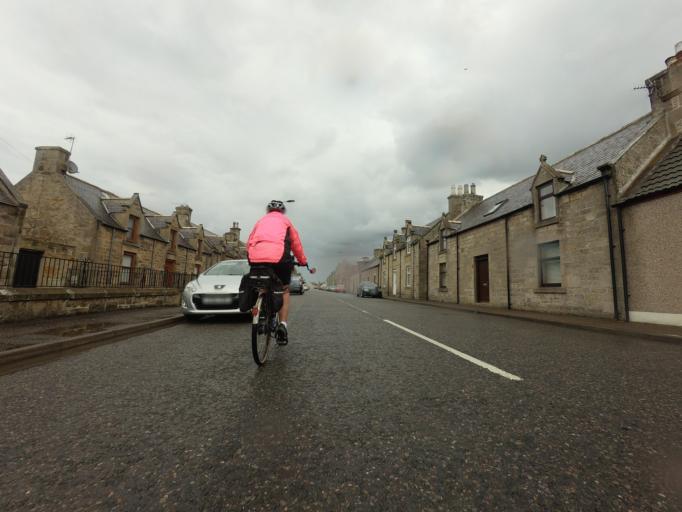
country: GB
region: Scotland
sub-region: Moray
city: Buckie
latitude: 57.6743
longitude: -2.9841
